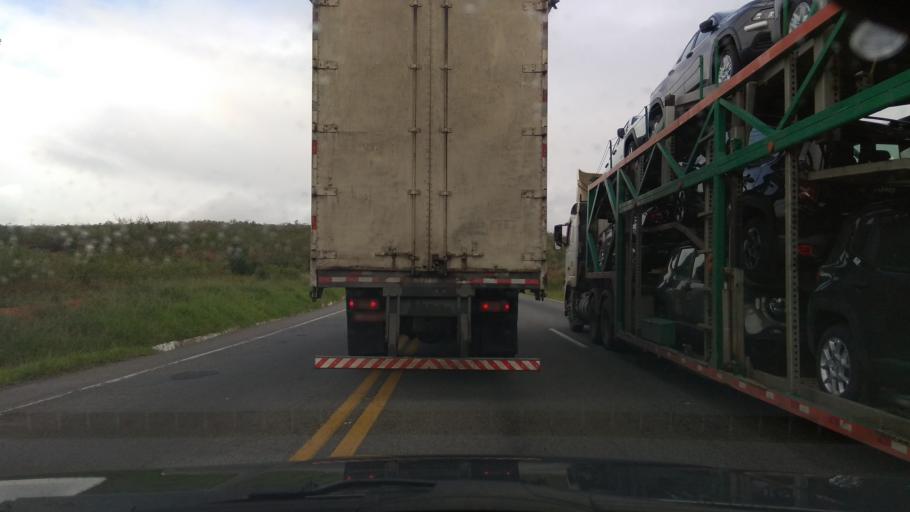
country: BR
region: Bahia
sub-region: Santa Ines
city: Santa Ines
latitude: -13.0420
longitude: -39.9676
